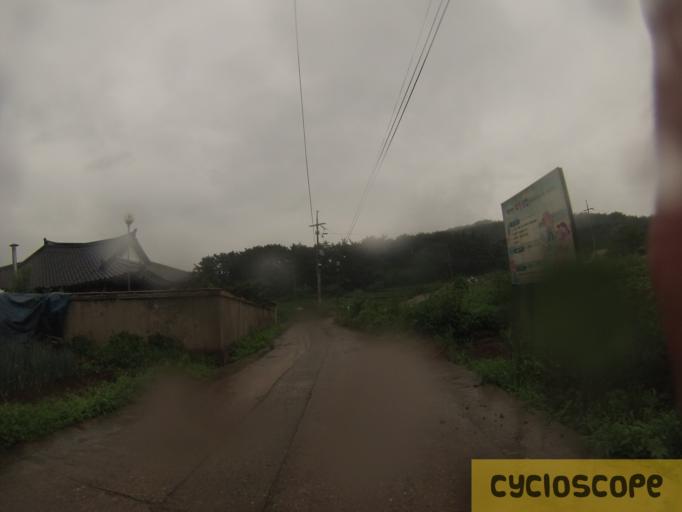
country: KR
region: Jeollabuk-do
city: Kunsan
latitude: 36.0590
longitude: 126.6618
